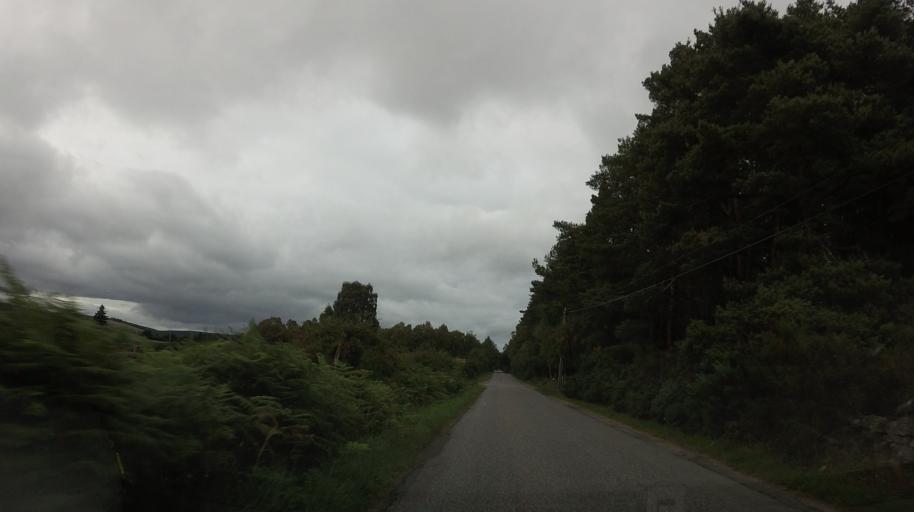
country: GB
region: Scotland
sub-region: Aberdeenshire
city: Banchory
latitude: 57.0706
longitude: -2.4655
